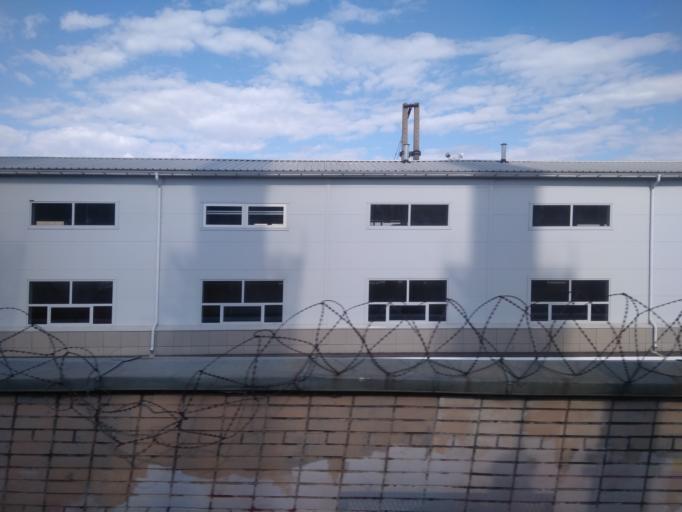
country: RU
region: Moscow
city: Mar'ina Roshcha
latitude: 55.7857
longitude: 37.6430
